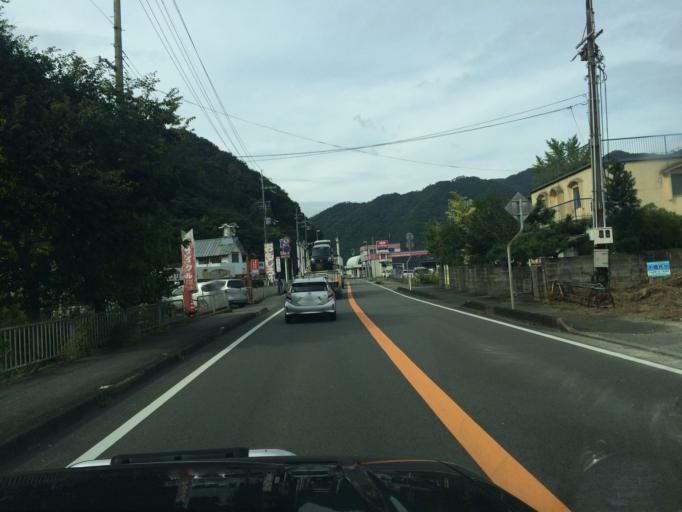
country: JP
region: Hyogo
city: Toyooka
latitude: 35.3501
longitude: 134.8357
